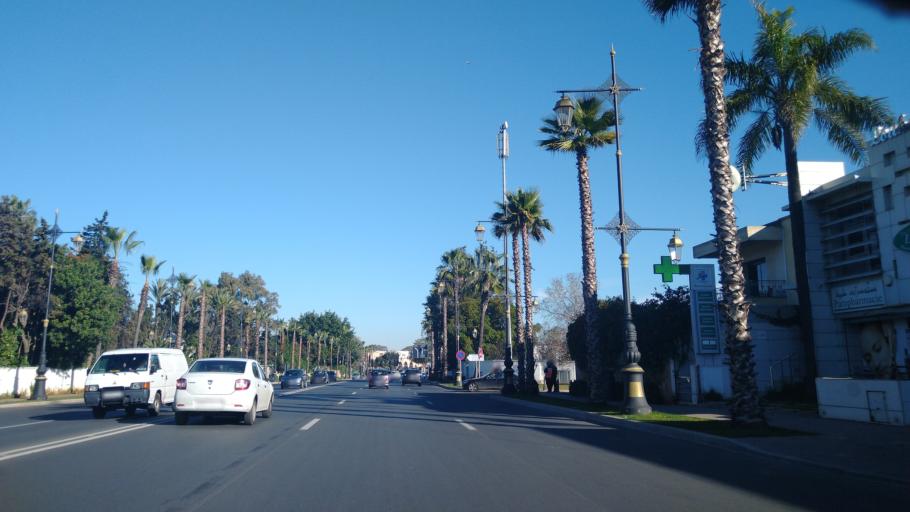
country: MA
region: Rabat-Sale-Zemmour-Zaer
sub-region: Rabat
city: Rabat
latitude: 34.0026
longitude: -6.8272
